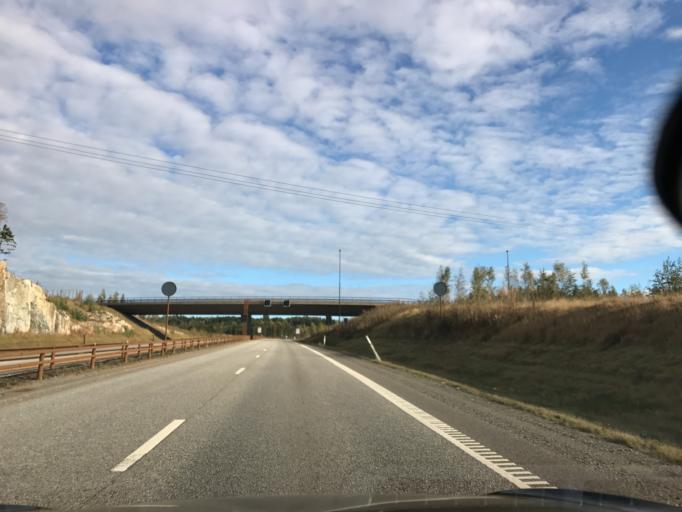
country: NO
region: Akershus
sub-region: Eidsvoll
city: Raholt
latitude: 60.3304
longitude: 11.1893
